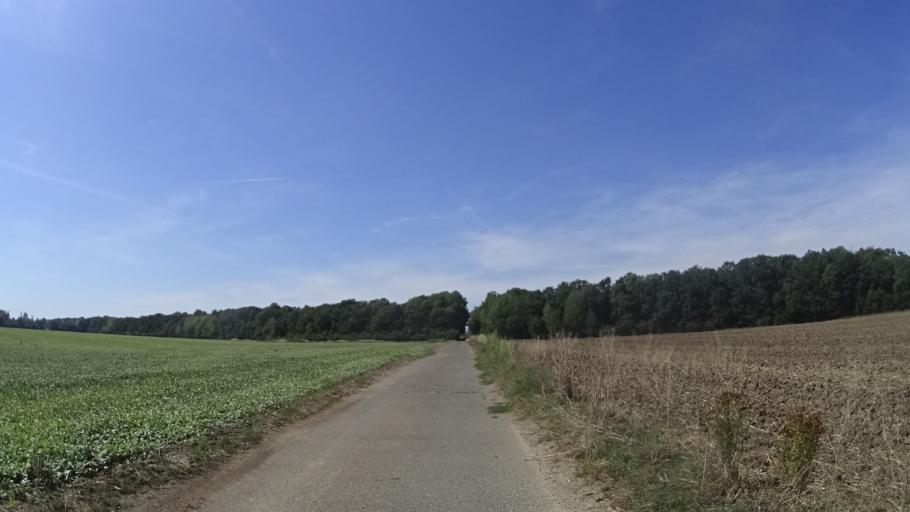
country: AT
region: Lower Austria
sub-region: Politischer Bezirk Ganserndorf
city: Angern an der March
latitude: 48.3688
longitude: 16.8608
